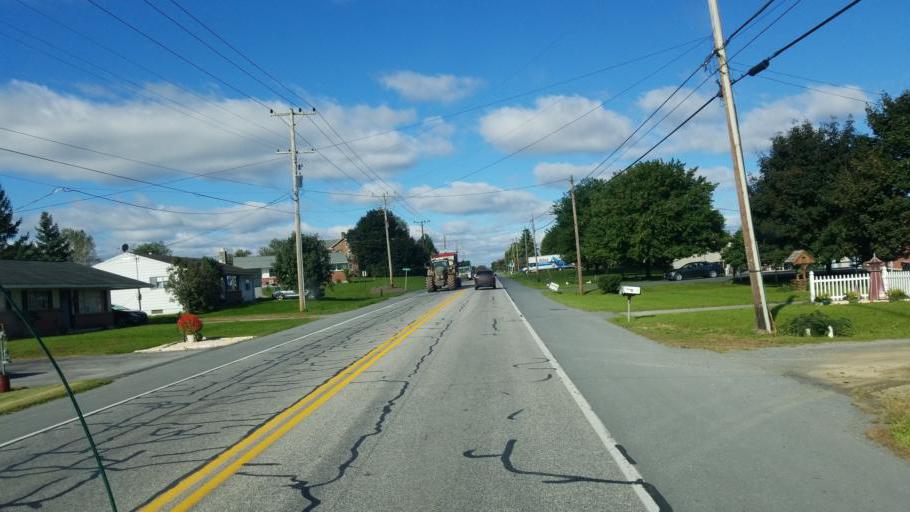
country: US
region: Pennsylvania
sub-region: Franklin County
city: Greencastle
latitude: 39.7977
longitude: -77.7697
